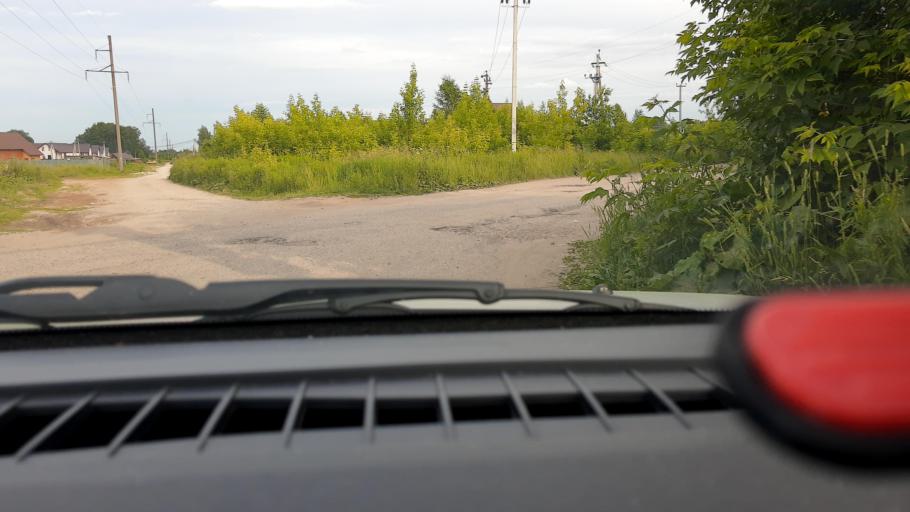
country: RU
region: Nizjnij Novgorod
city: Neklyudovo
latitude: 56.4074
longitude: 44.0145
